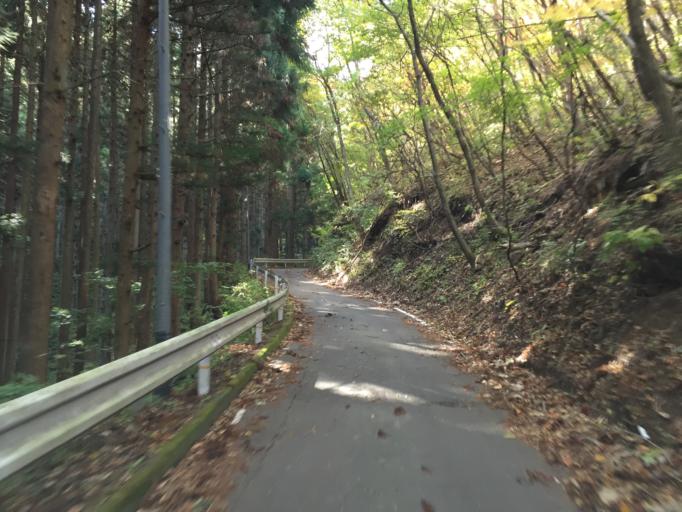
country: JP
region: Fukushima
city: Fukushima-shi
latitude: 37.7351
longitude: 140.3325
